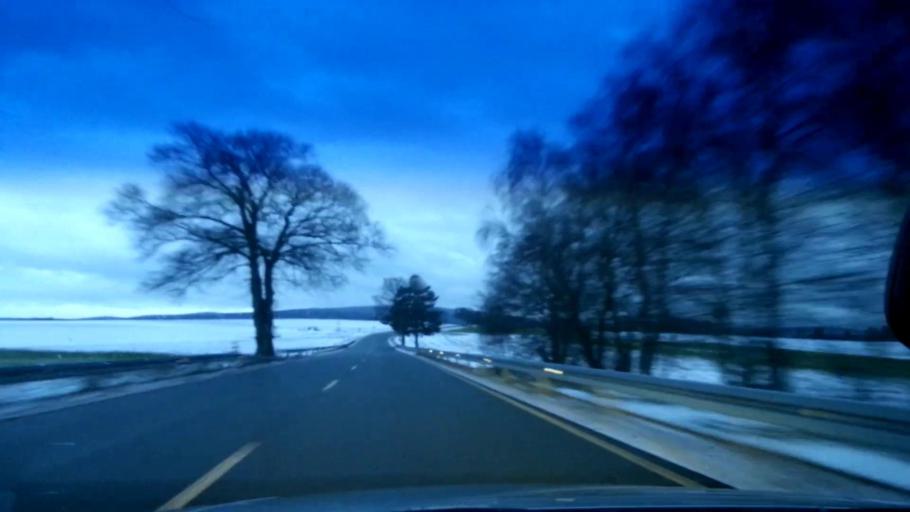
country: DE
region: Bavaria
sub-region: Upper Franconia
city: Weissenstadt
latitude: 50.1148
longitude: 11.8992
